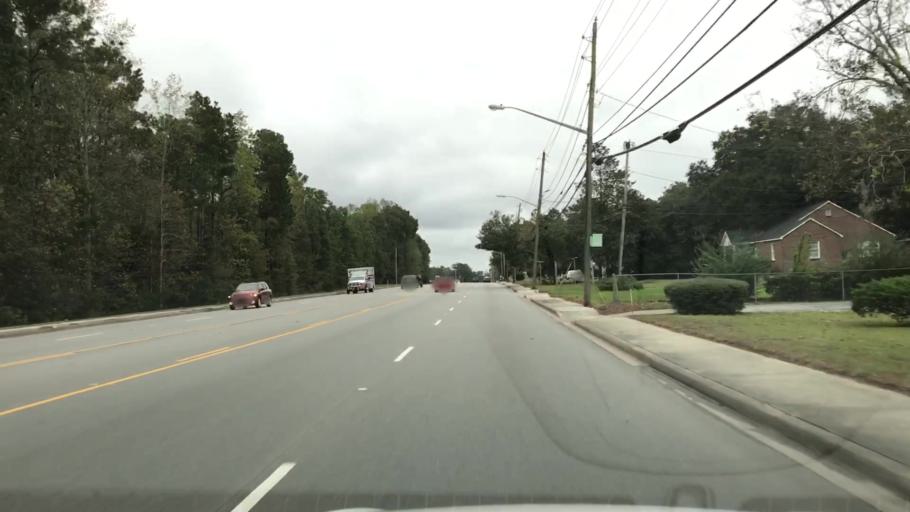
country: US
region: South Carolina
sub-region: Georgetown County
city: Georgetown
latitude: 33.3399
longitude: -79.3030
